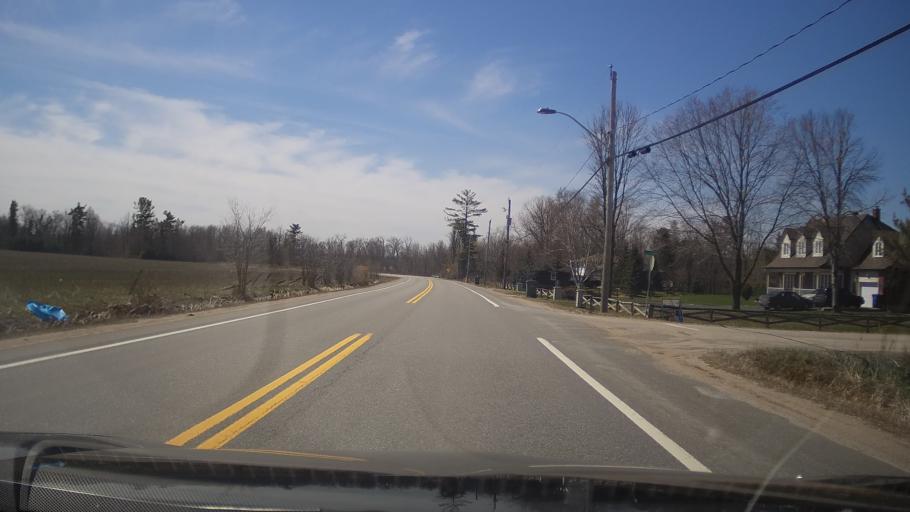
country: CA
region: Ontario
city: Bells Corners
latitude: 45.4831
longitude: -75.9529
